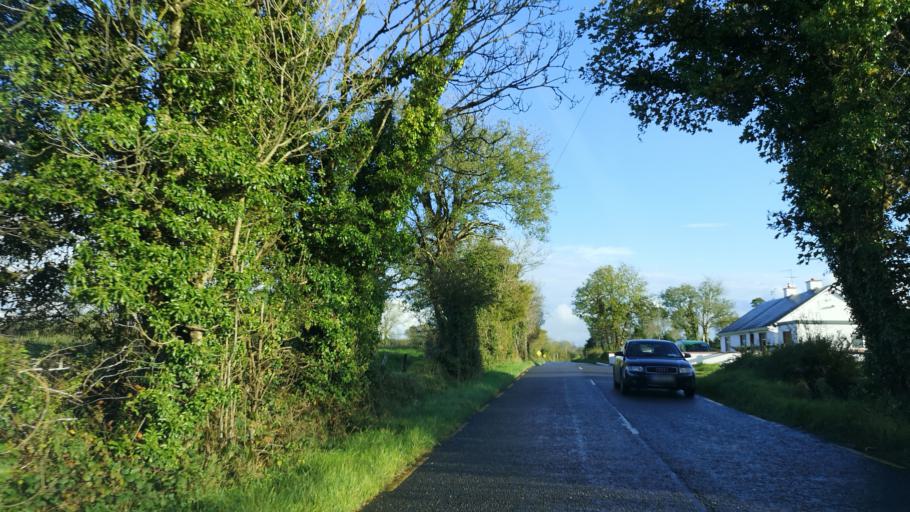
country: IE
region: Connaught
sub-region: Roscommon
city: Castlerea
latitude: 53.7959
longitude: -8.4905
